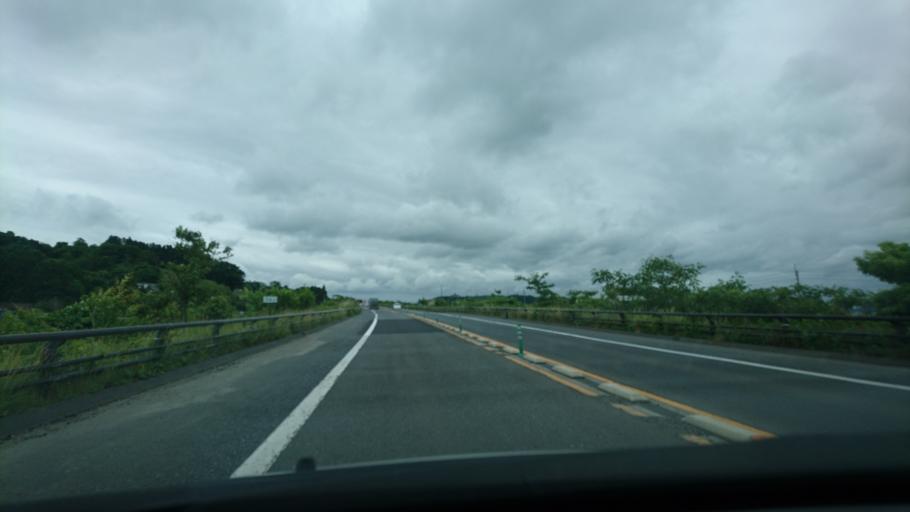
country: JP
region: Miyagi
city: Wakuya
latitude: 38.5840
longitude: 141.2751
